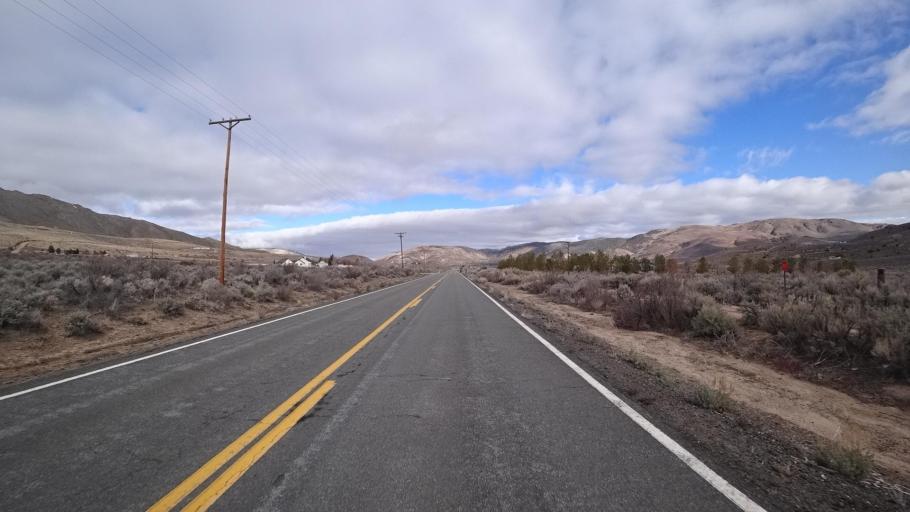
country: US
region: Nevada
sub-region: Washoe County
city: Cold Springs
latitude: 39.8755
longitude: -119.9643
